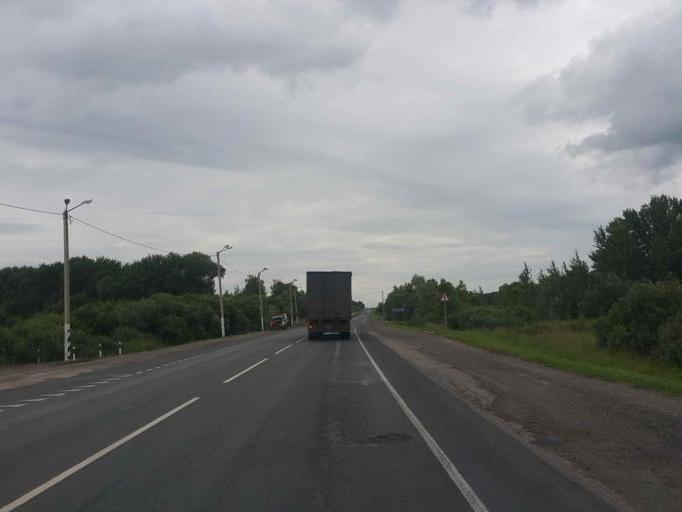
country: RU
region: Tambov
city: Zavoronezhskoye
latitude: 52.9278
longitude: 40.6161
